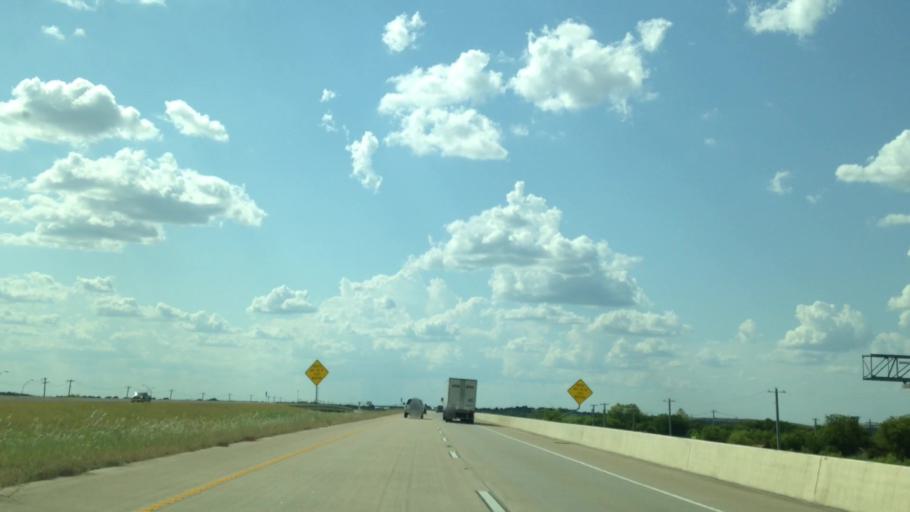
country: US
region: Texas
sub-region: Travis County
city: Onion Creek
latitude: 30.0824
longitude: -97.7319
